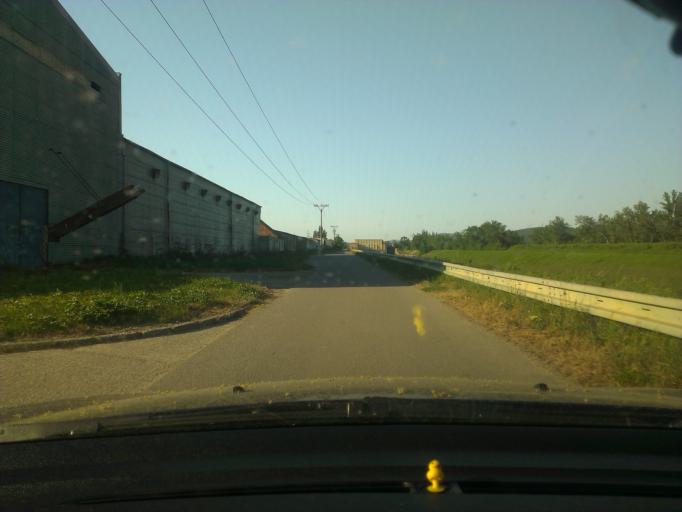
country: SK
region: Trnavsky
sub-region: Okres Trnava
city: Piestany
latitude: 48.6535
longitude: 17.8516
